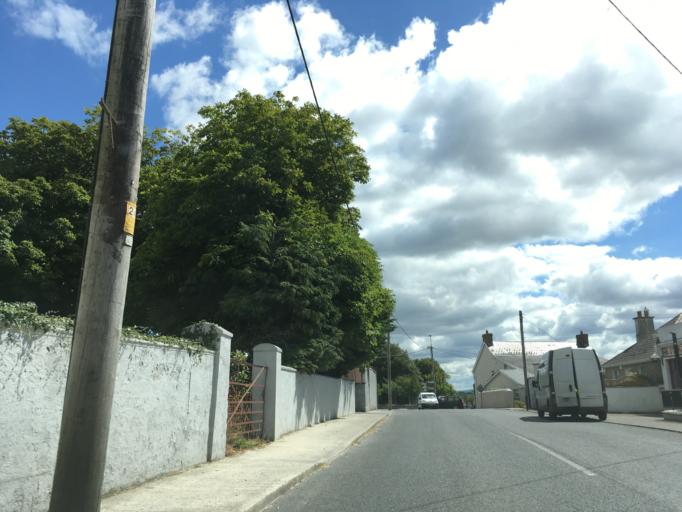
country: IE
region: Munster
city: Cahir
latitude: 52.4411
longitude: -7.8834
